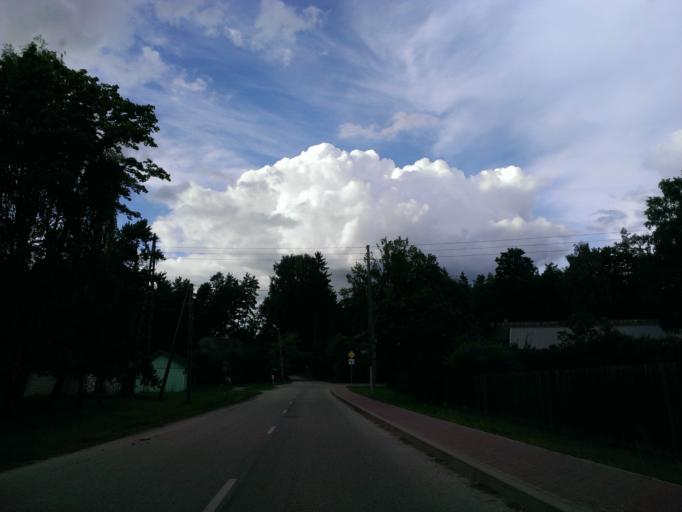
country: LV
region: Ikskile
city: Ikskile
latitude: 56.8369
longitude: 24.4874
